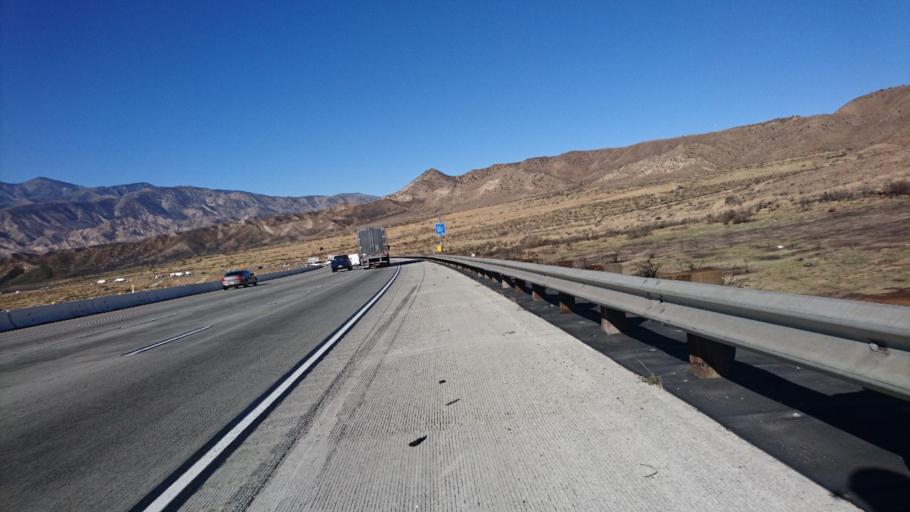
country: US
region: California
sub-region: San Bernardino County
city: Oak Hills
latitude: 34.3475
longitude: -117.4692
